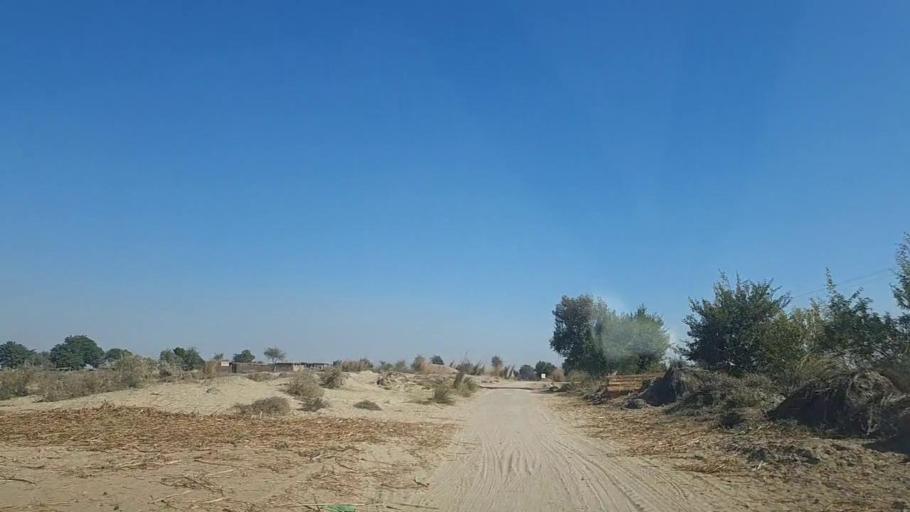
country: PK
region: Sindh
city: Khadro
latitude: 26.2093
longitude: 68.8762
